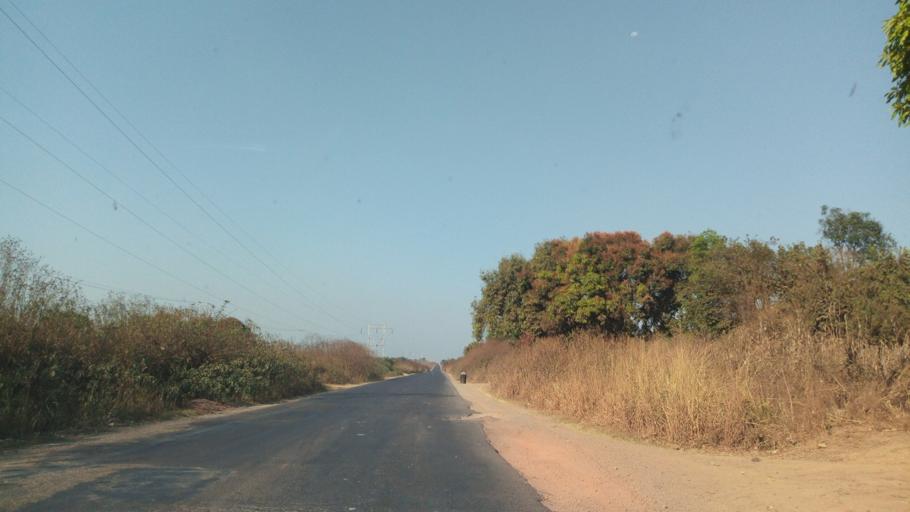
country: CD
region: Katanga
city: Likasi
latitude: -11.0027
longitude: 26.8512
